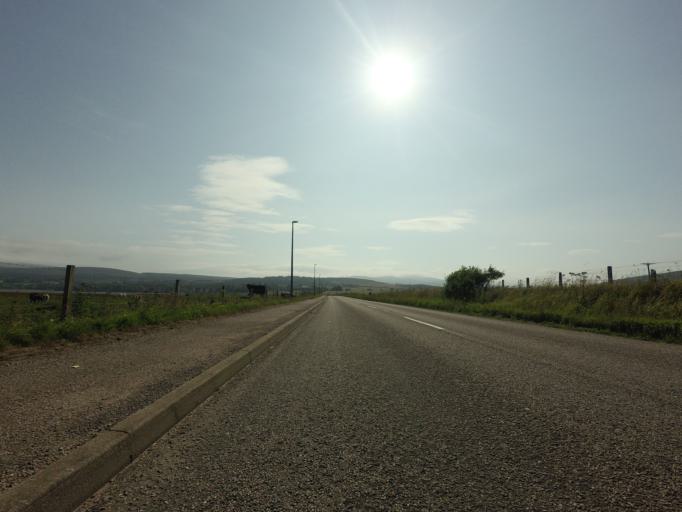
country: GB
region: Scotland
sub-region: Highland
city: Alness
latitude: 57.8889
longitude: -4.3550
